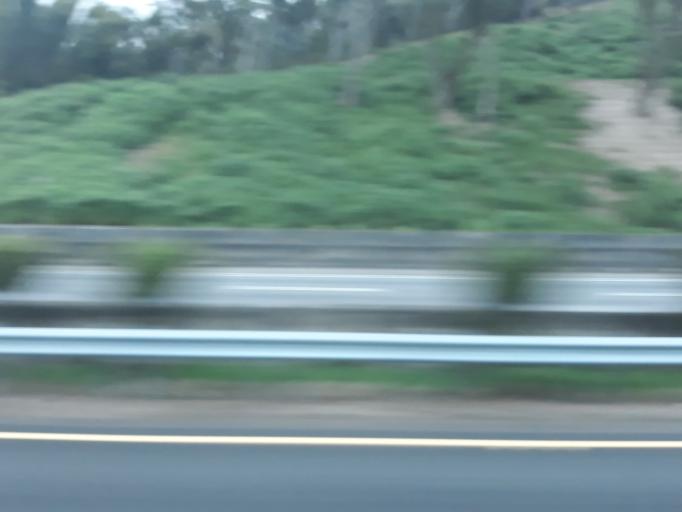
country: TW
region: Taiwan
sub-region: Miaoli
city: Miaoli
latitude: 24.6150
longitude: 120.8635
